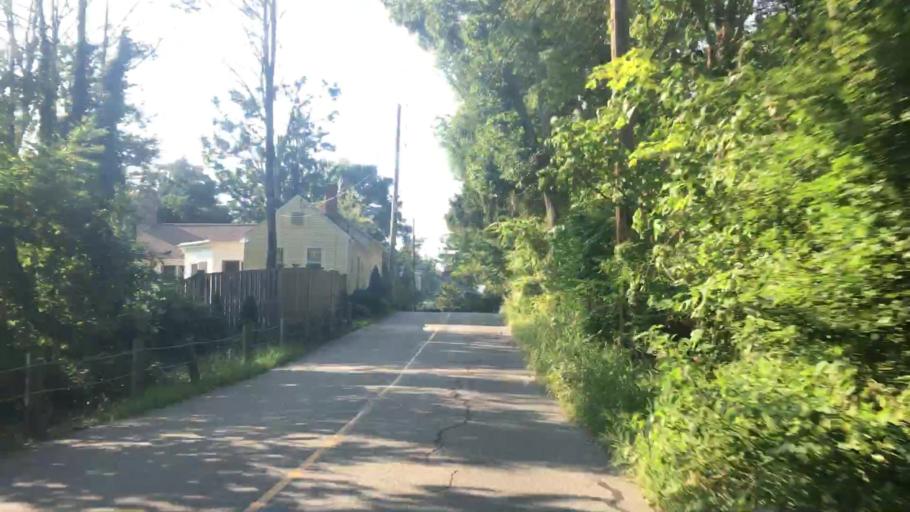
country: US
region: Connecticut
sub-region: Middlesex County
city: Chester Center
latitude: 41.3999
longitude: -72.4581
